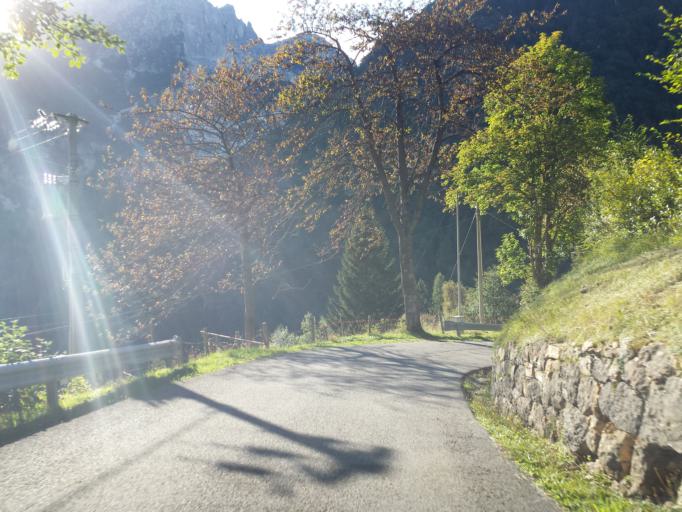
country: IT
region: Veneto
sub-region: Provincia di Vicenza
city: Recoaro Terme
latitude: 45.7193
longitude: 11.1781
